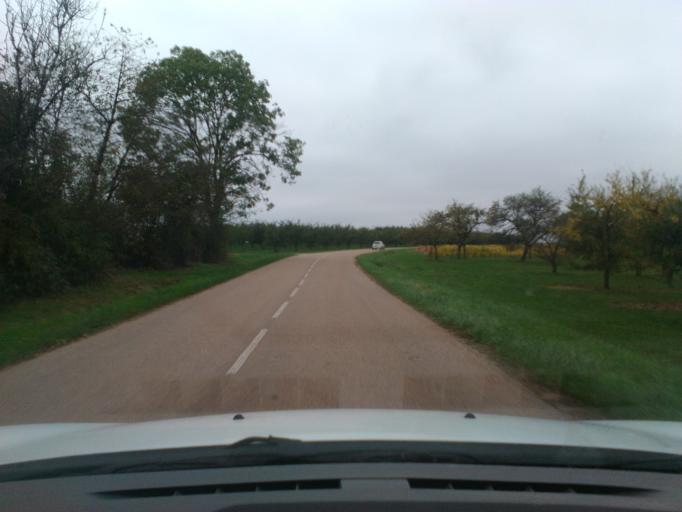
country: FR
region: Lorraine
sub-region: Departement des Vosges
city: Charmes
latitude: 48.3007
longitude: 6.2586
